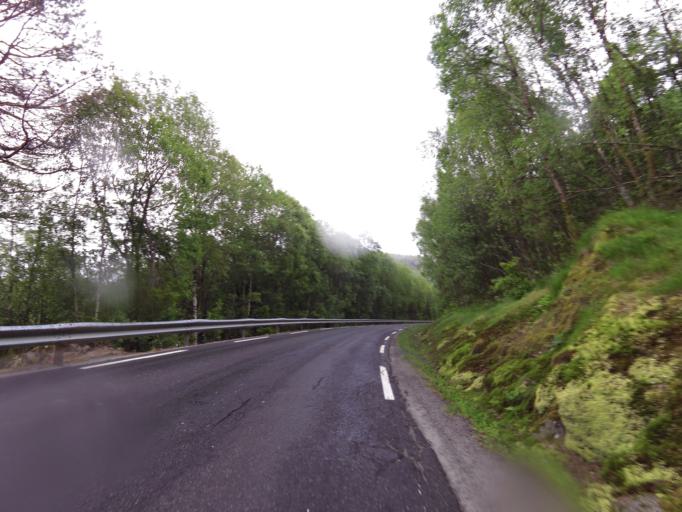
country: NO
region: Vest-Agder
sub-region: Lyngdal
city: Lyngdal
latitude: 58.1149
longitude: 7.0775
